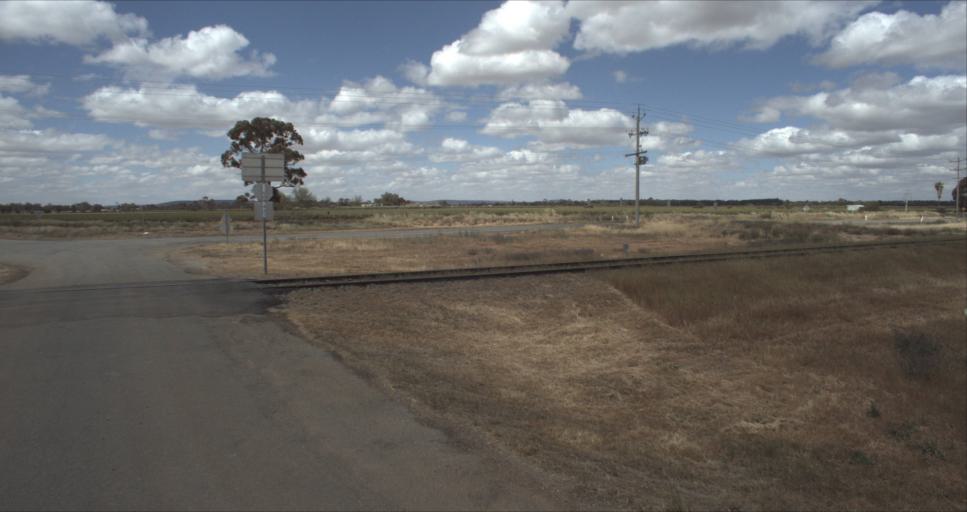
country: AU
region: New South Wales
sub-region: Leeton
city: Leeton
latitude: -34.5789
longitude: 146.3974
